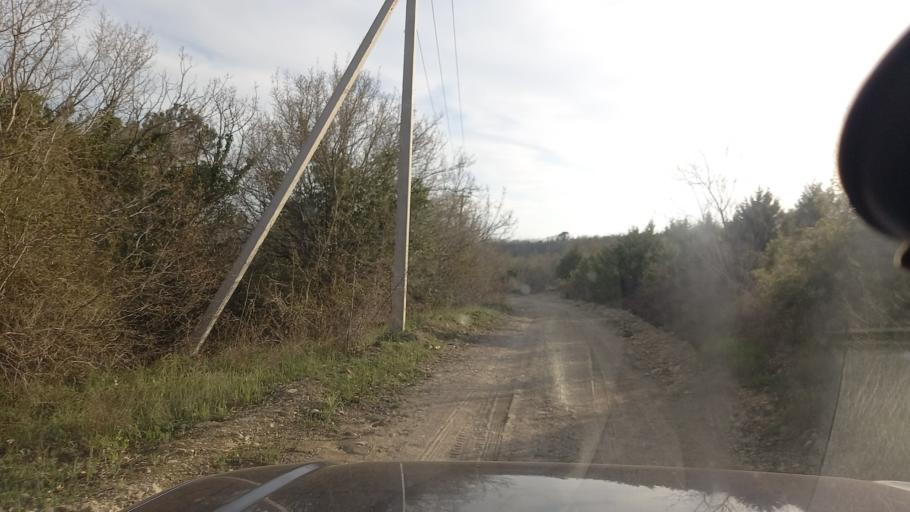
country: RU
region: Krasnodarskiy
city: Arkhipo-Osipovka
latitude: 44.3633
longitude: 38.5745
